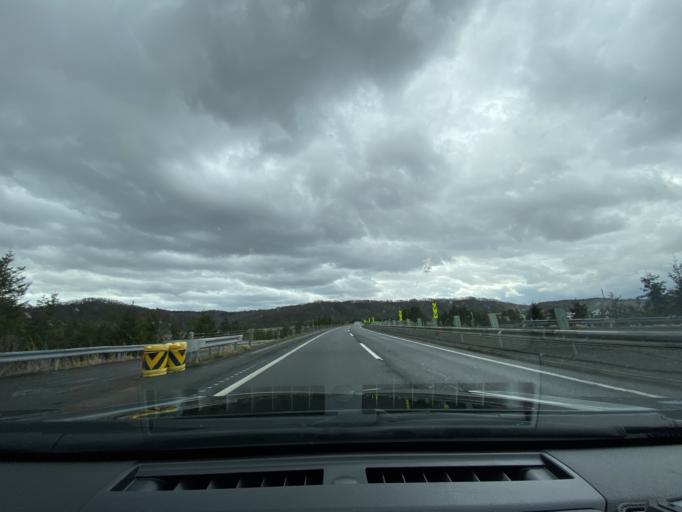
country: JP
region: Hokkaido
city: Takikawa
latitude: 43.5572
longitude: 141.9546
